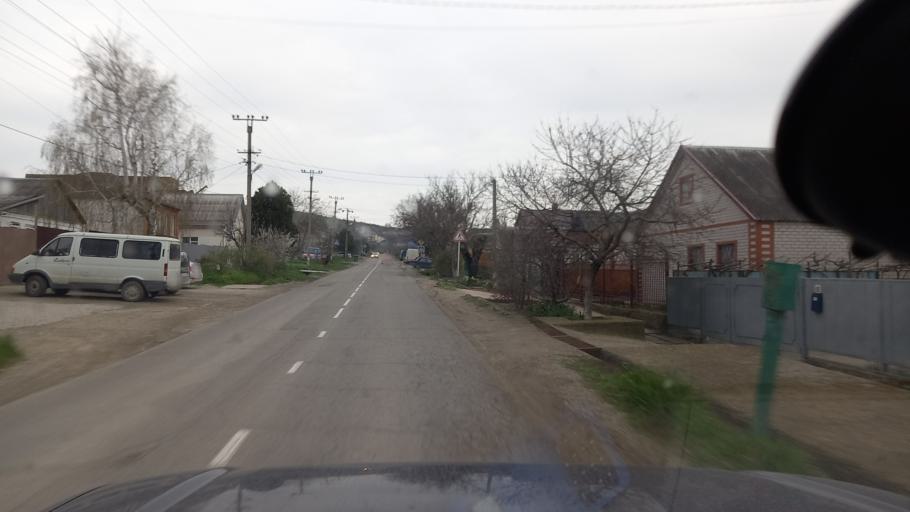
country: RU
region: Krasnodarskiy
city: Sukko
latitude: 44.8510
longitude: 37.4363
